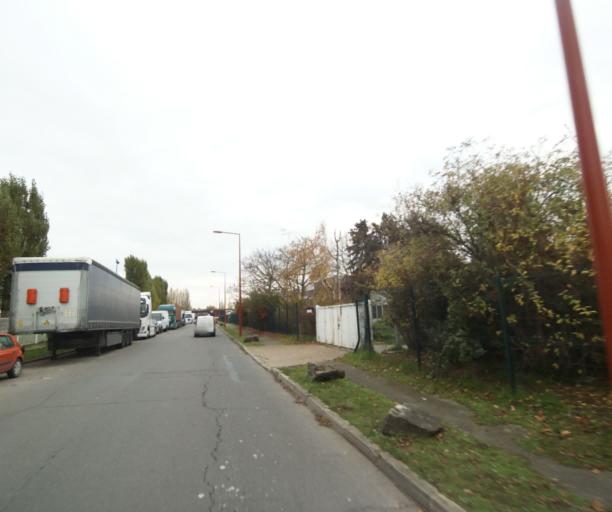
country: FR
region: Ile-de-France
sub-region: Departement du Val-d'Oise
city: Gonesse
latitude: 48.9810
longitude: 2.4583
